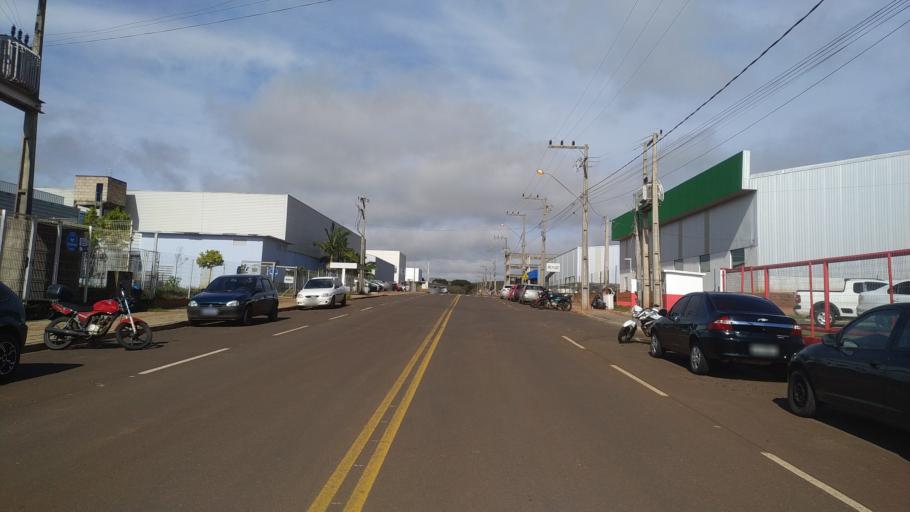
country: BR
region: Santa Catarina
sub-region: Chapeco
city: Chapeco
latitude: -27.1577
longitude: -52.6004
